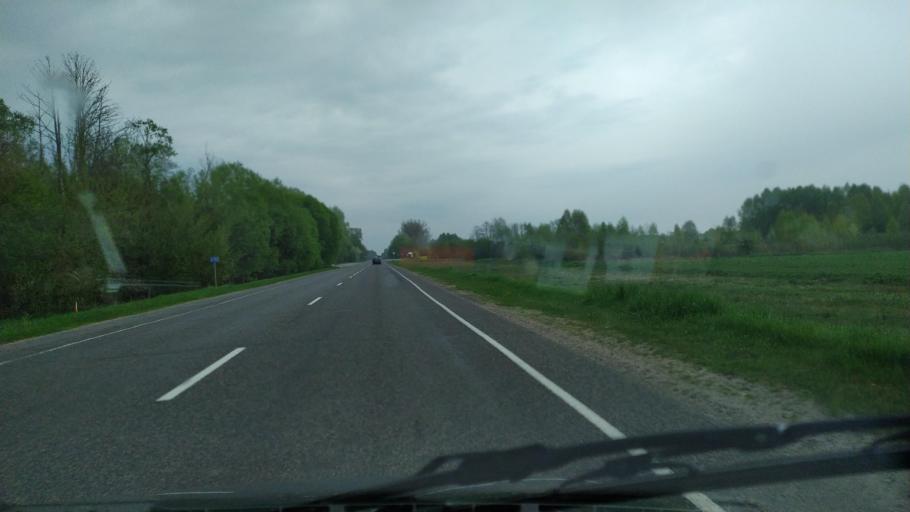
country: BY
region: Brest
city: Horad Kobryn
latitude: 52.2899
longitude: 24.4990
